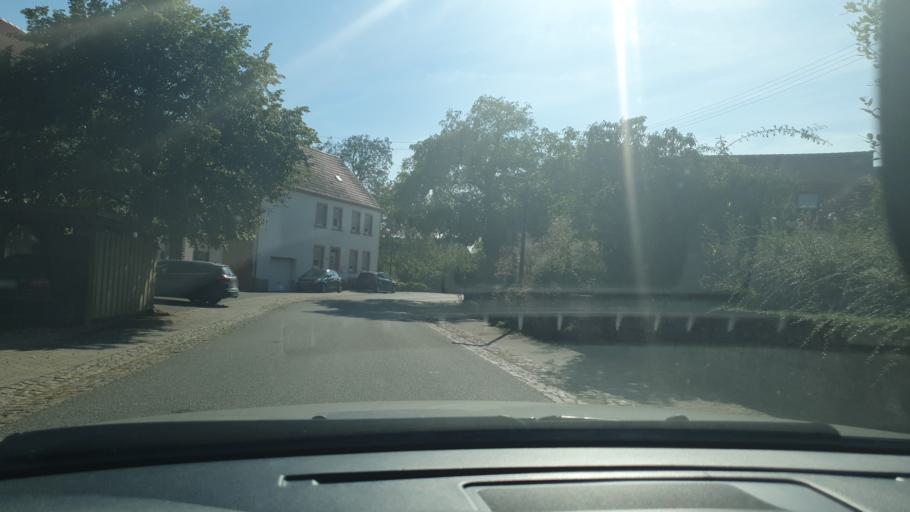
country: DE
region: Rheinland-Pfalz
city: Kleinbundenbach
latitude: 49.3112
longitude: 7.4411
